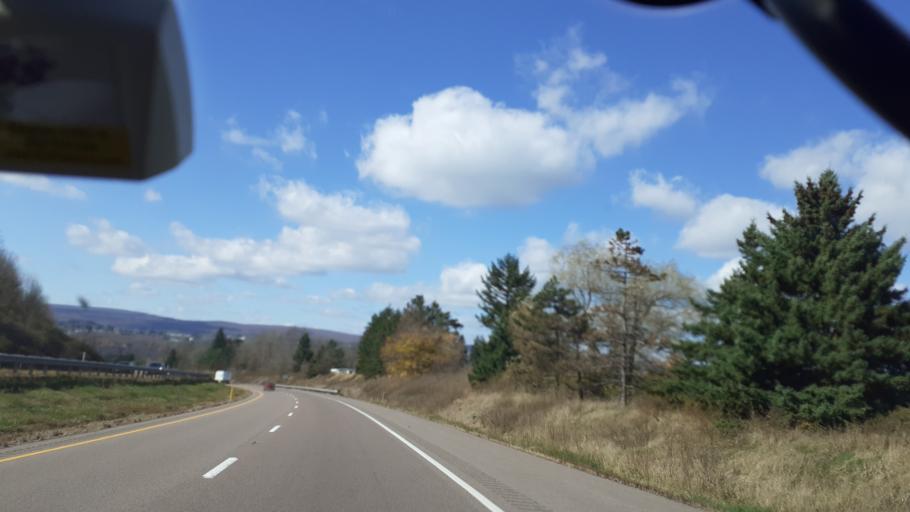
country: US
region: Pennsylvania
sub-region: Somerset County
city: Meyersdale
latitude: 39.6945
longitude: -79.1204
